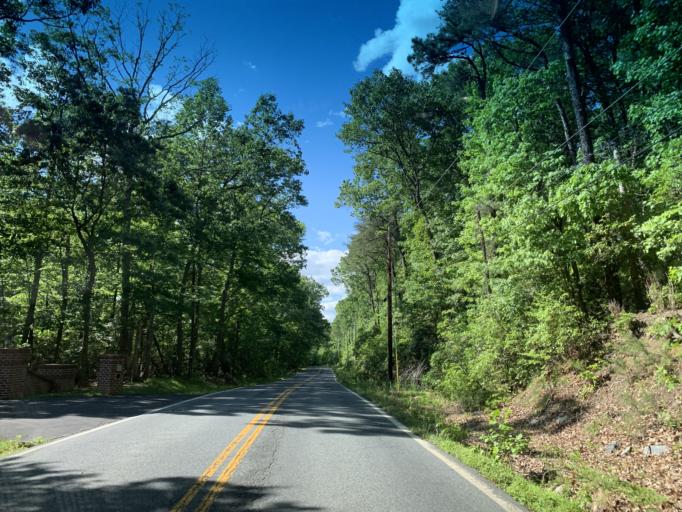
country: US
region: Maryland
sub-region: Cecil County
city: North East
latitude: 39.5610
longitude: -75.9339
